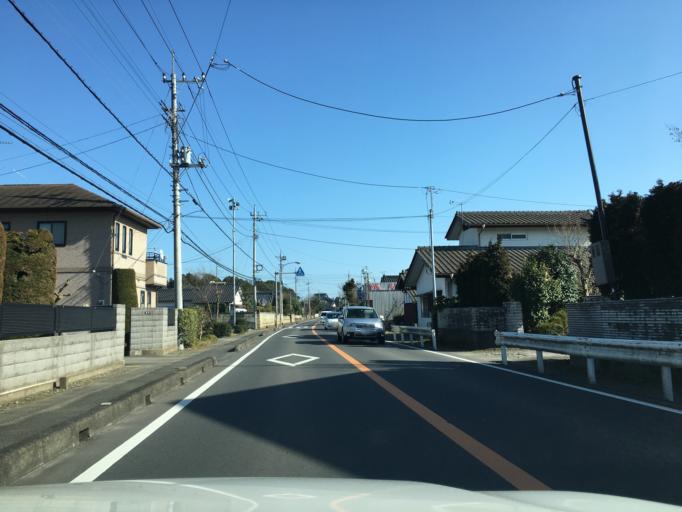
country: JP
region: Ibaraki
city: Omiya
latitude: 36.4596
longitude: 140.4041
